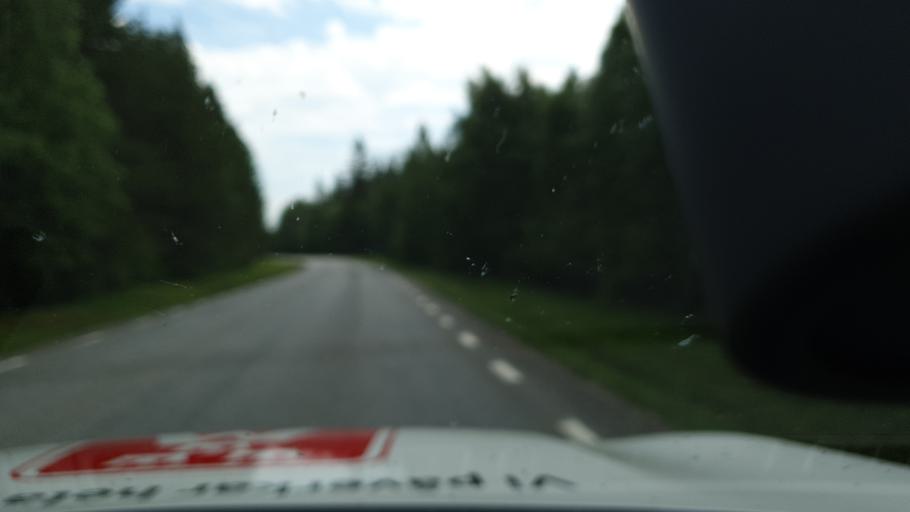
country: SE
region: Vaesterbotten
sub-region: Robertsfors Kommun
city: Robertsfors
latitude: 64.2039
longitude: 20.8197
